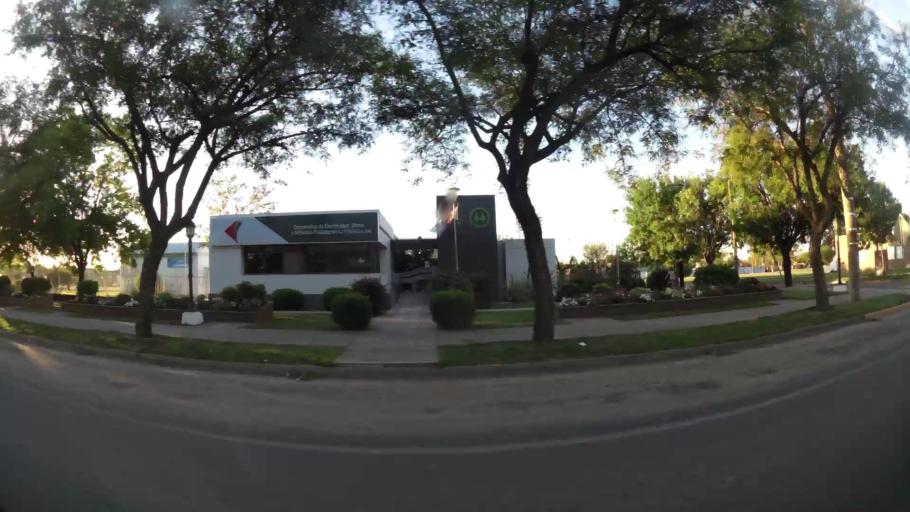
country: AR
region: Cordoba
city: La Playosa
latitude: -32.1010
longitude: -63.0327
